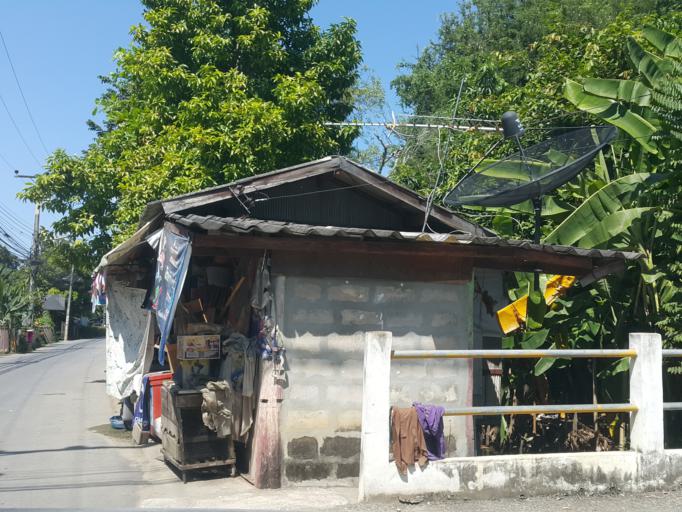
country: TH
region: Chiang Mai
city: Saraphi
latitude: 18.7606
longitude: 99.0468
